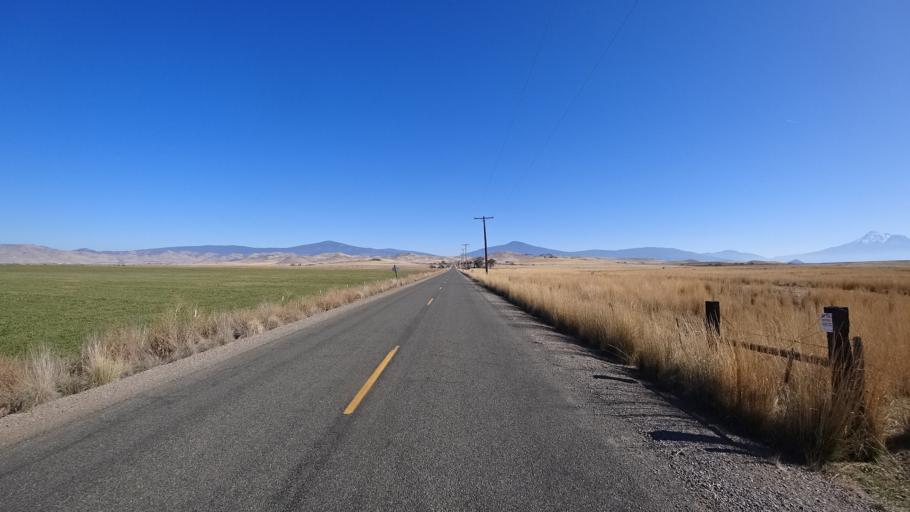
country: US
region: California
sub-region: Siskiyou County
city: Montague
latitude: 41.7560
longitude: -122.4837
